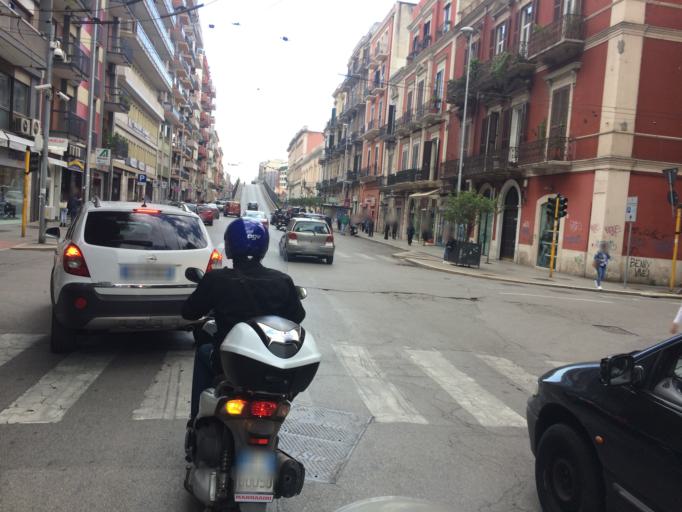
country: IT
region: Apulia
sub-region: Provincia di Bari
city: Bari
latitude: 41.1202
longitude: 16.8727
